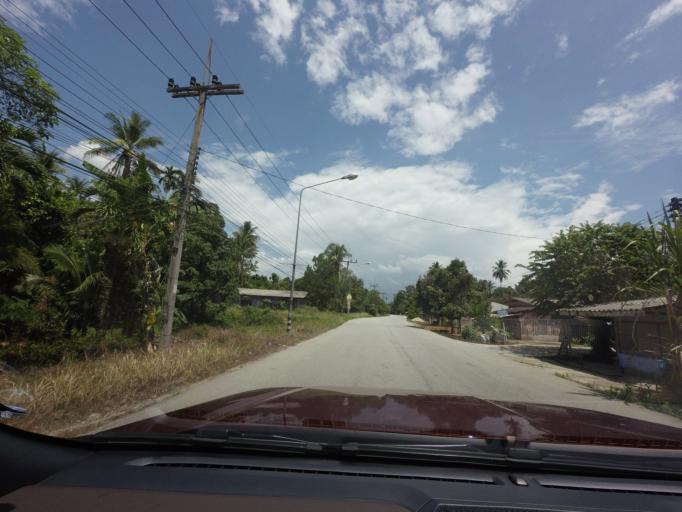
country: TH
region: Narathiwat
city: Chanae
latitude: 6.0963
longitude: 101.6917
